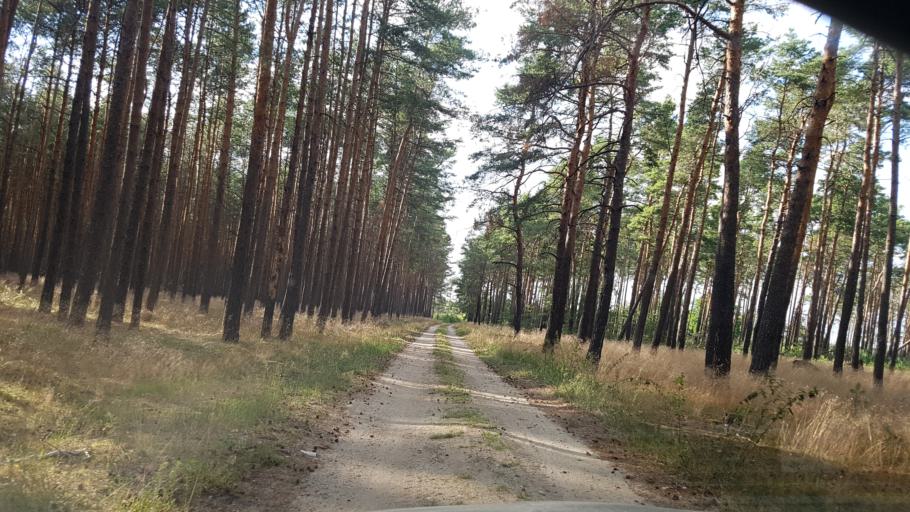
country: DE
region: Brandenburg
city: Schilda
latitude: 51.6348
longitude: 13.4025
